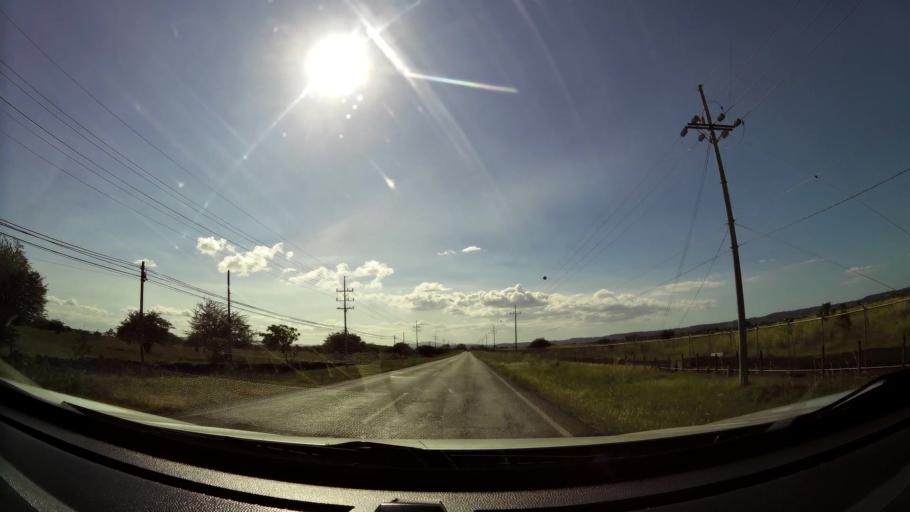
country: CR
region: Guanacaste
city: Sardinal
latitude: 10.5867
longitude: -85.5550
